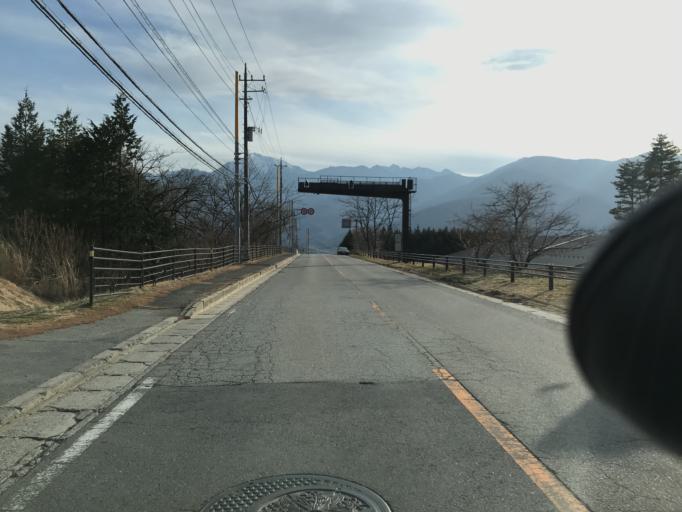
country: JP
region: Nagano
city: Chino
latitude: 35.8690
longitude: 138.3084
